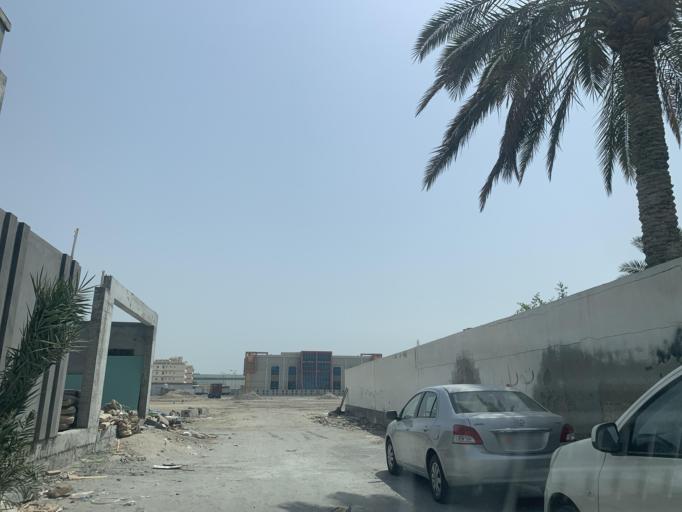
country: BH
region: Northern
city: Madinat `Isa
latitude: 26.1866
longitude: 50.5518
